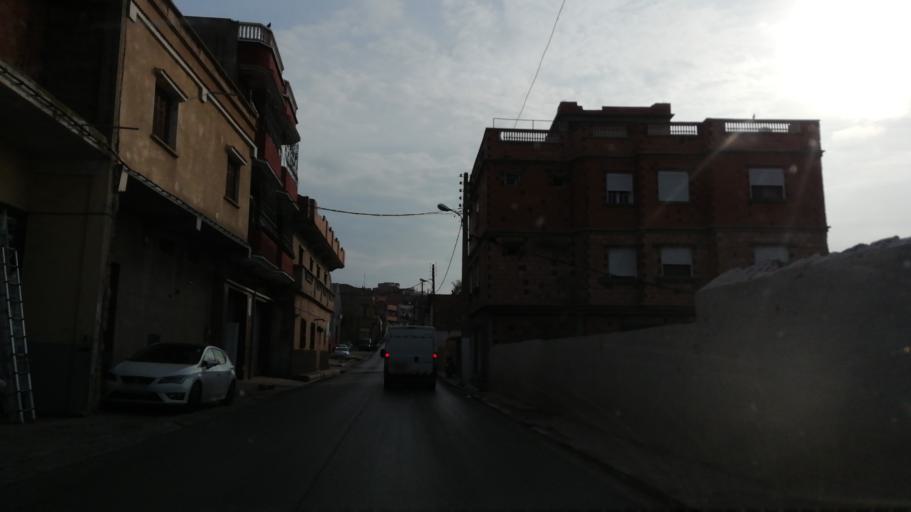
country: DZ
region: Mostaganem
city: Mostaganem
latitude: 35.9017
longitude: 0.0754
